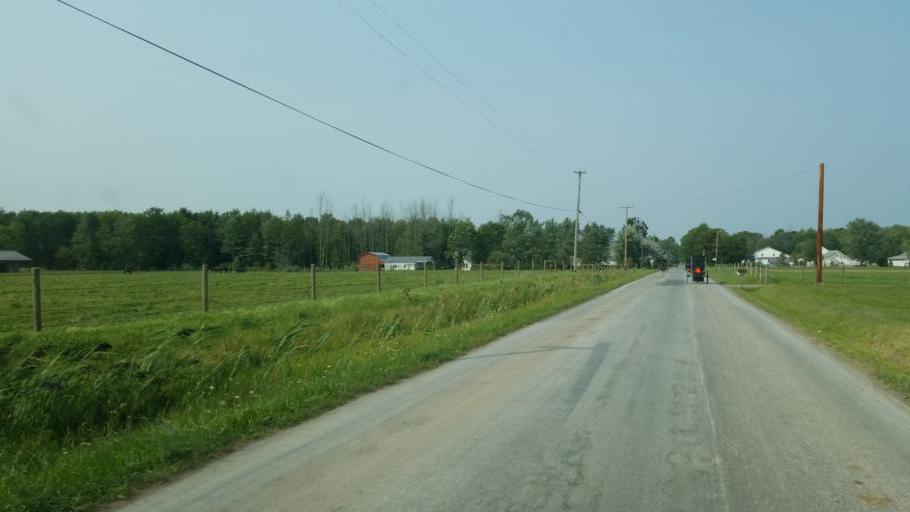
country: US
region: Ohio
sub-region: Geauga County
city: Middlefield
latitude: 41.4950
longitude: -81.0031
